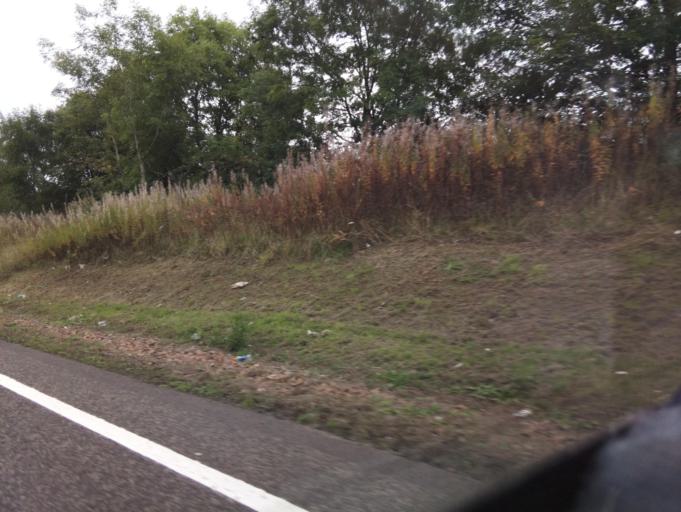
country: GB
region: Scotland
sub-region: Fife
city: Kennoway
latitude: 56.1924
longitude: -3.0681
